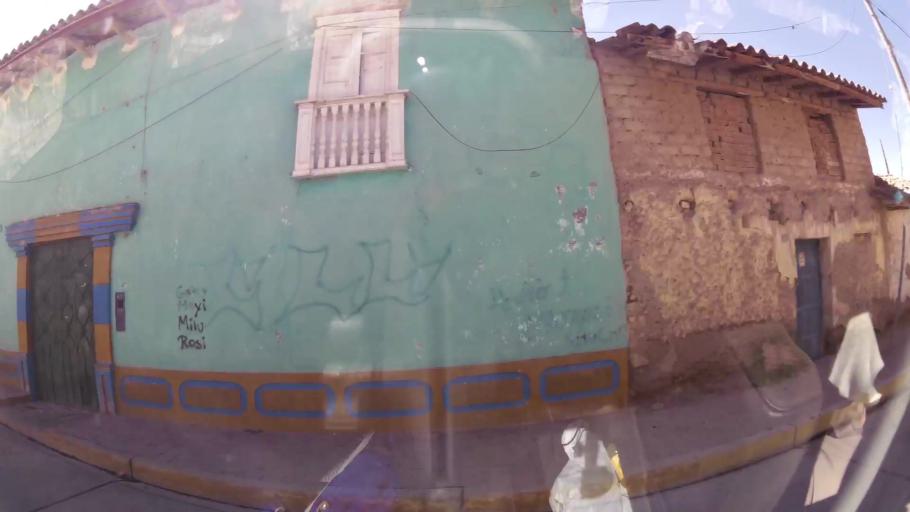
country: PE
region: Junin
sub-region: Provincia de Jauja
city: Jauja
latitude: -11.7758
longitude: -75.5028
